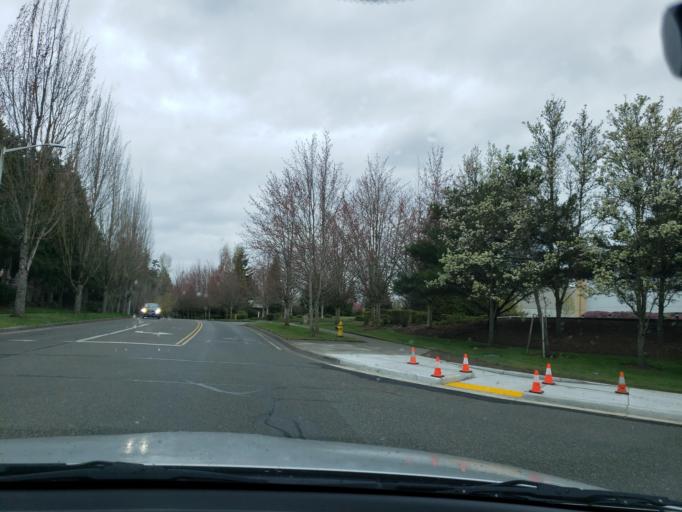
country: US
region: Washington
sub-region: Snohomish County
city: Meadowdale
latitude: 47.8914
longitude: -122.2969
